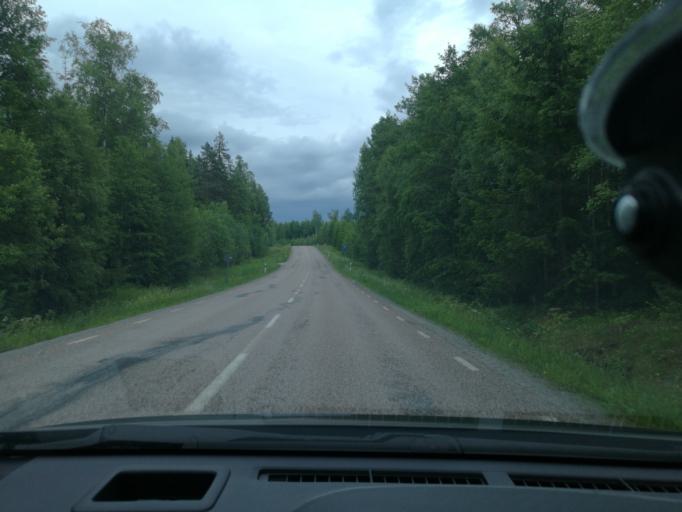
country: SE
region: Vaestmanland
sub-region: Vasteras
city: Skultuna
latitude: 59.9093
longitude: 16.3987
